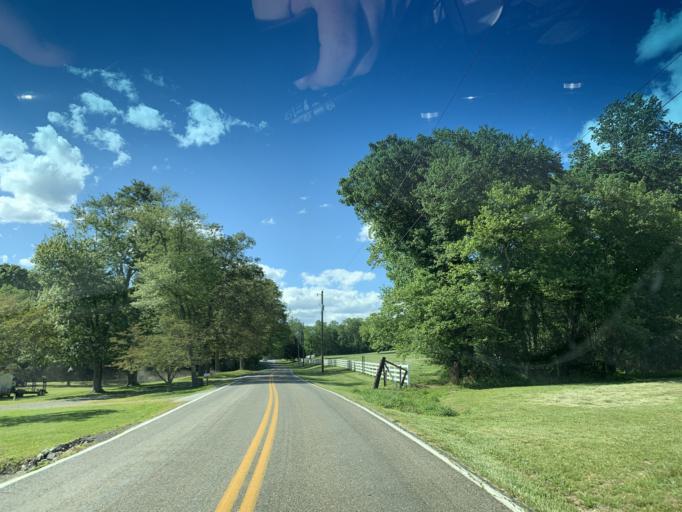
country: US
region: Maryland
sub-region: Cecil County
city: North East
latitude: 39.5477
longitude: -75.9197
